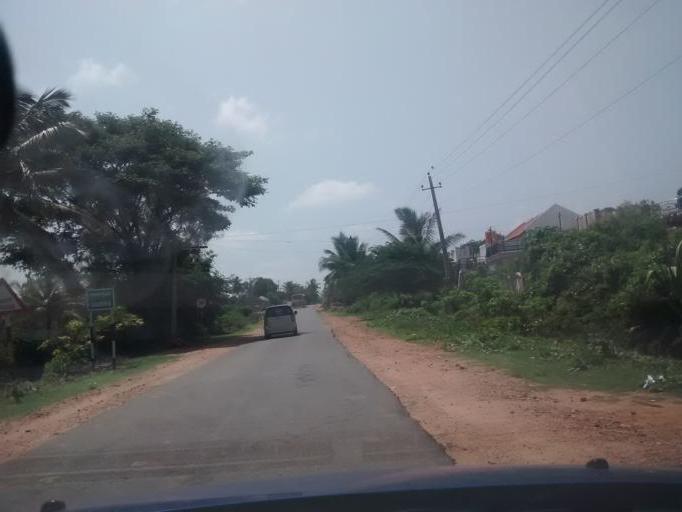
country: IN
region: Karnataka
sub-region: Hassan
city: Konanur
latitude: 12.5638
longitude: 76.2528
